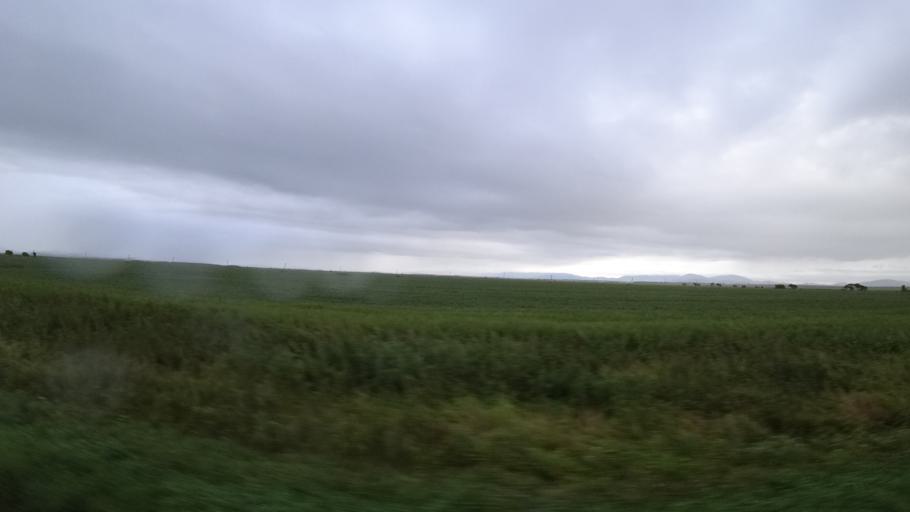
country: RU
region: Primorskiy
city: Chernigovka
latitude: 44.3848
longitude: 132.5295
